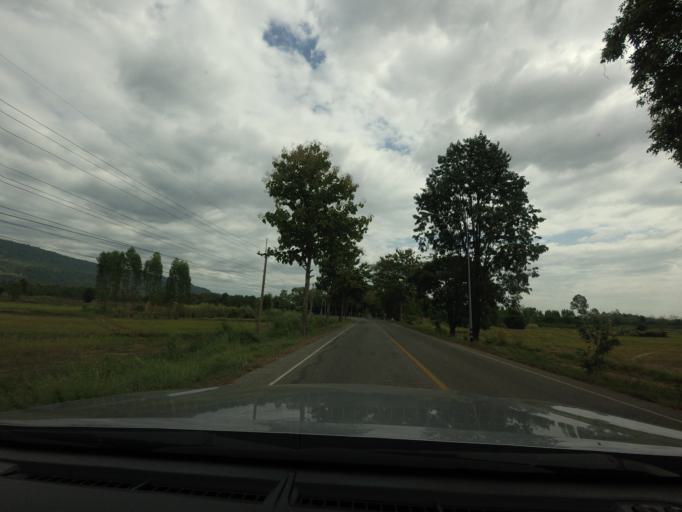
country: TH
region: Phitsanulok
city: Wang Thong
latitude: 16.7054
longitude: 100.4969
